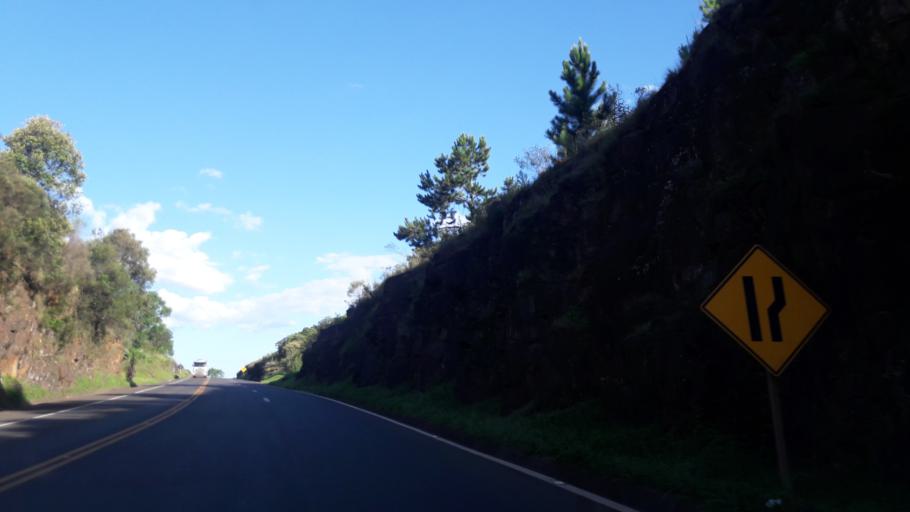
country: BR
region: Parana
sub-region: Guarapuava
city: Guarapuava
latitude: -25.3585
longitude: -51.3573
